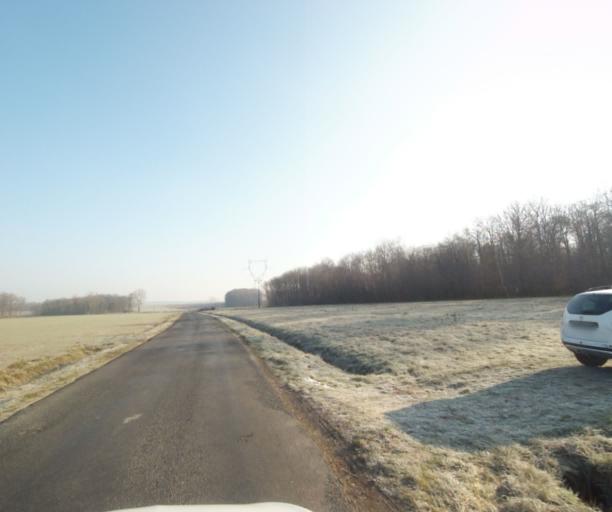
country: FR
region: Champagne-Ardenne
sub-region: Departement de la Haute-Marne
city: Montier-en-Der
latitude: 48.5066
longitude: 4.7428
